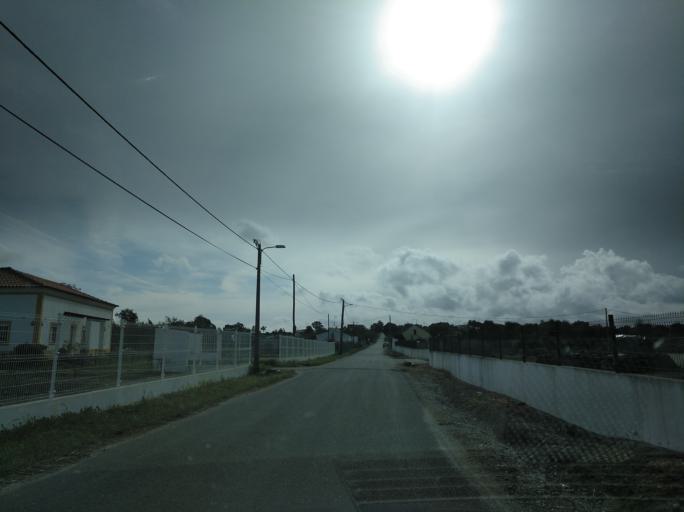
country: PT
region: Setubal
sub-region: Grandola
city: Grandola
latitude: 38.1987
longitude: -8.5464
